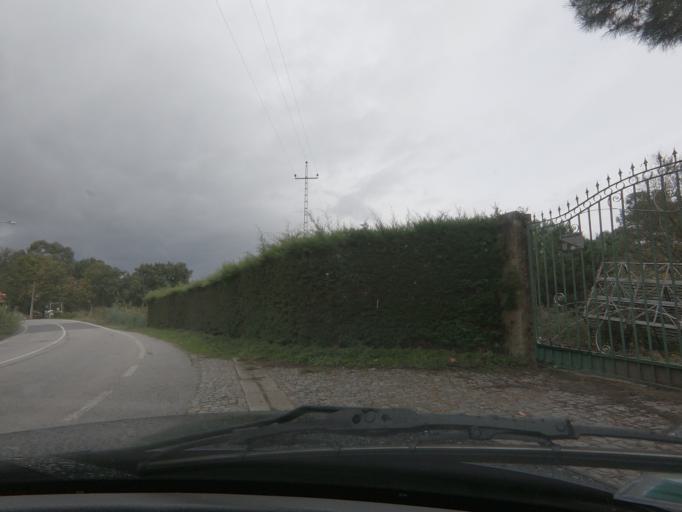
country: PT
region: Vila Real
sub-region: Mondim de Basto
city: Mondim de Basto
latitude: 41.3955
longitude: -7.9598
